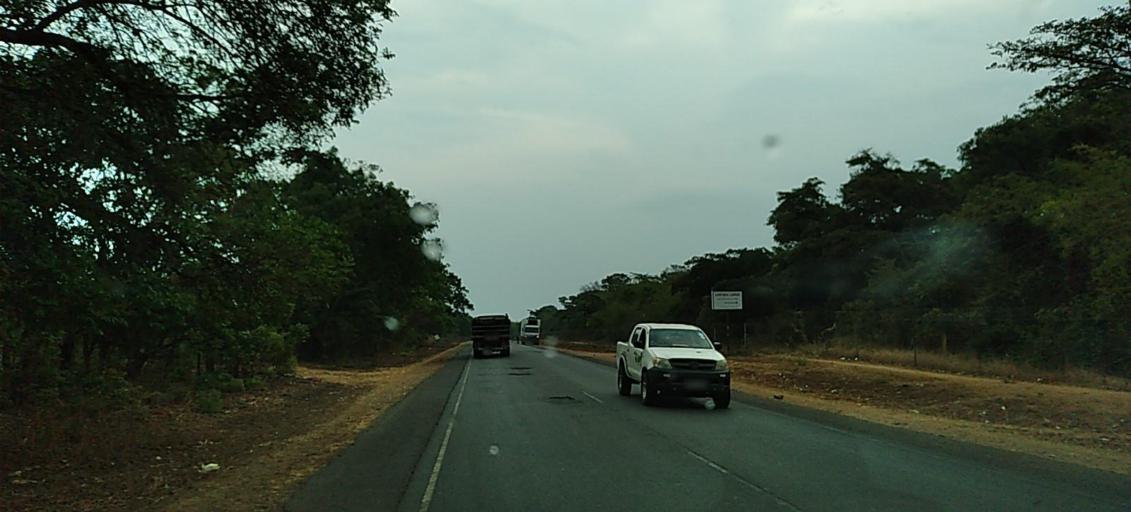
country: ZM
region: Copperbelt
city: Luanshya
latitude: -13.0587
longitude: 28.4584
